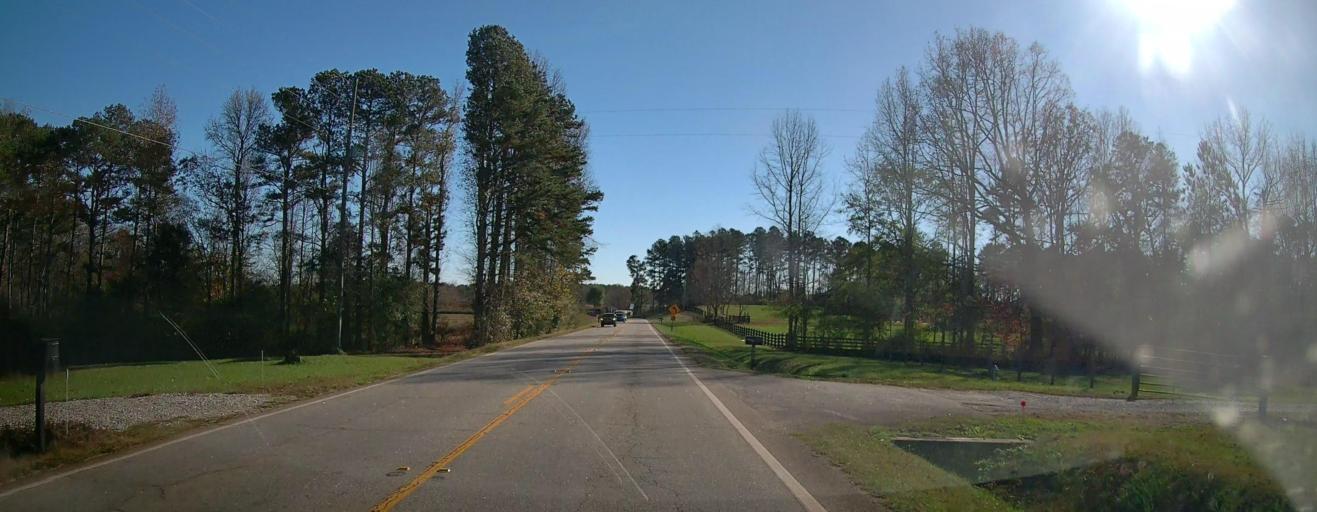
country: US
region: Georgia
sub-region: Hall County
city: Lula
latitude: 34.4473
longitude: -83.7276
